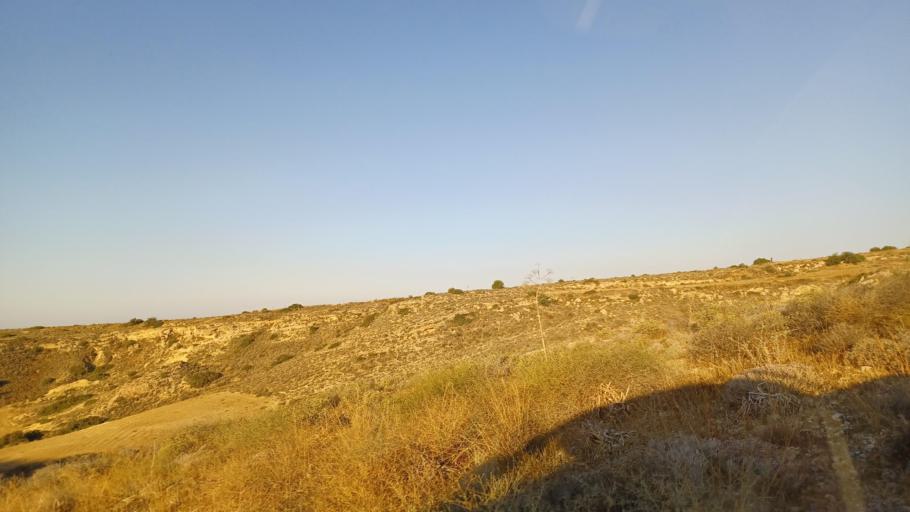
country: CY
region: Larnaka
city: Pyla
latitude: 34.9919
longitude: 33.7111
